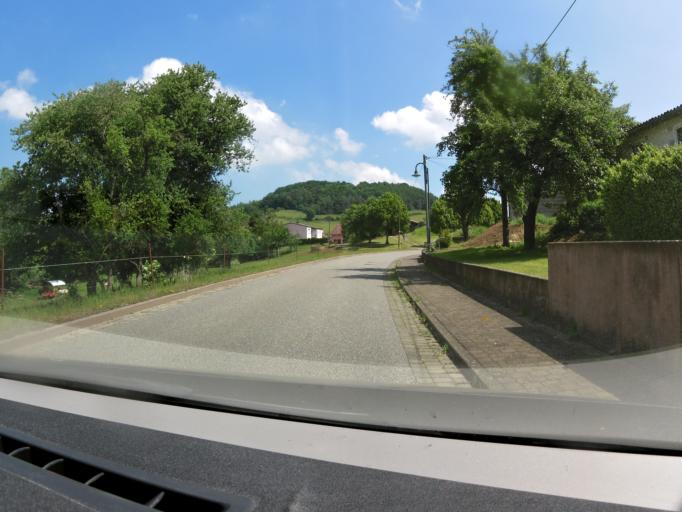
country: DE
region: Hesse
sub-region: Regierungsbezirk Kassel
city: Ronshausen
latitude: 50.9824
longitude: 9.8816
